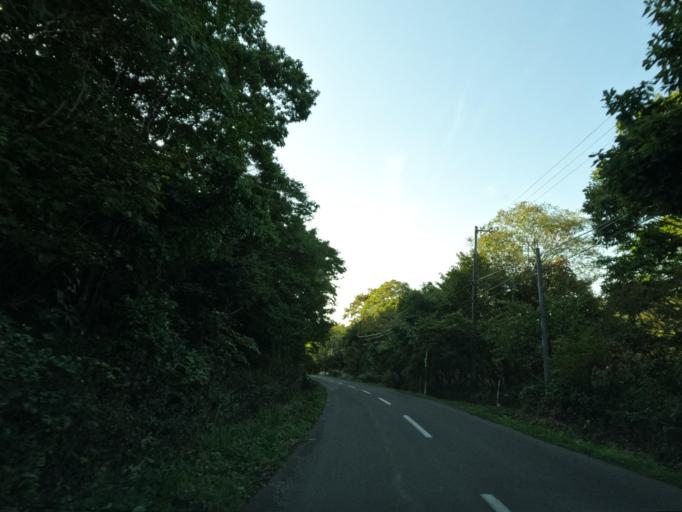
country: JP
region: Hokkaido
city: Date
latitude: 42.3995
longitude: 140.9307
